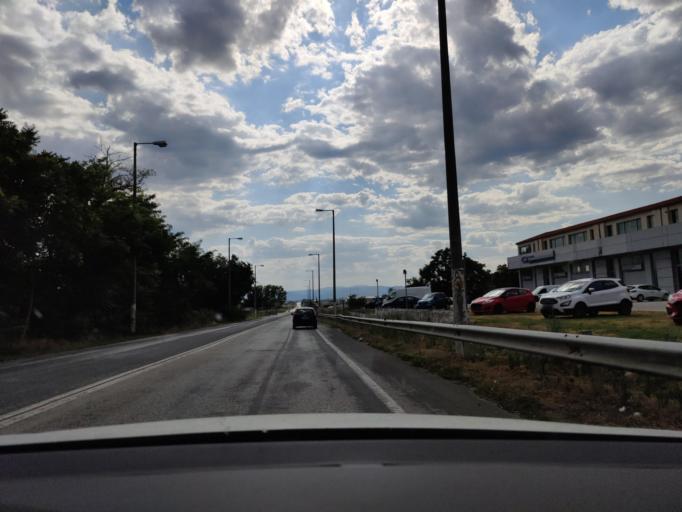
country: GR
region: Central Macedonia
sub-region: Nomos Serron
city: Lefkonas
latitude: 41.0985
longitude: 23.4807
